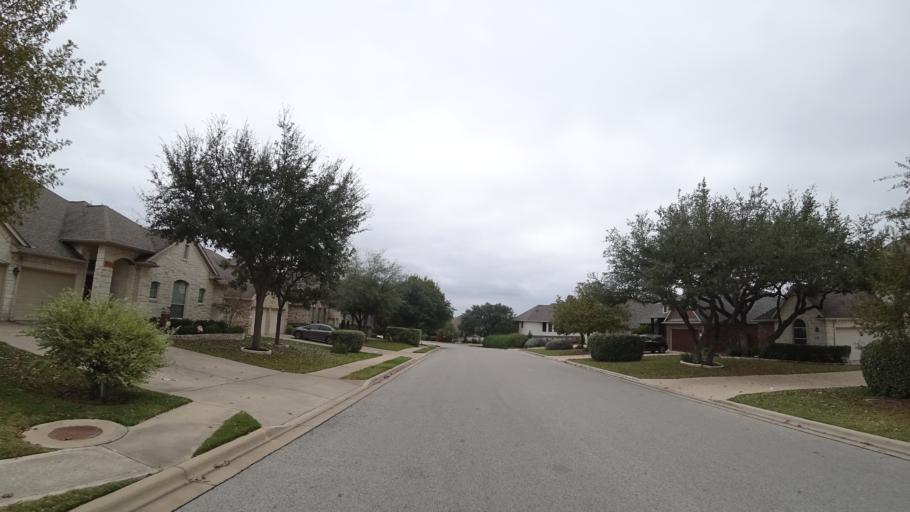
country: US
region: Texas
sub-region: Travis County
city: Bee Cave
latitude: 30.3533
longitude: -97.9050
